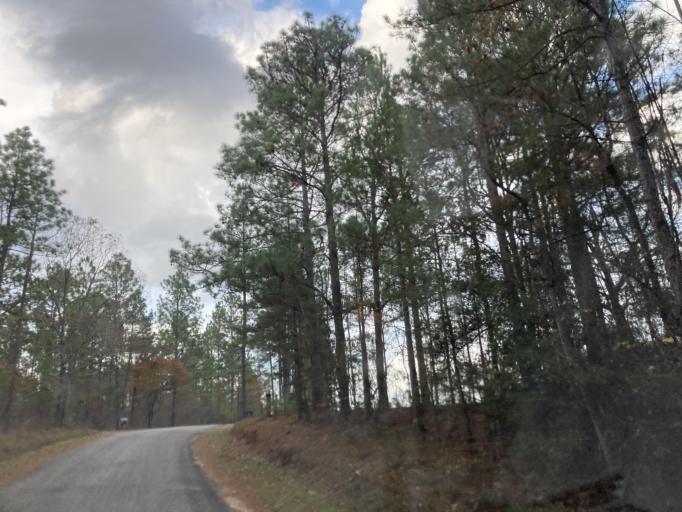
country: US
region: Mississippi
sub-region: Marion County
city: Columbia
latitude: 31.1829
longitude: -89.6472
